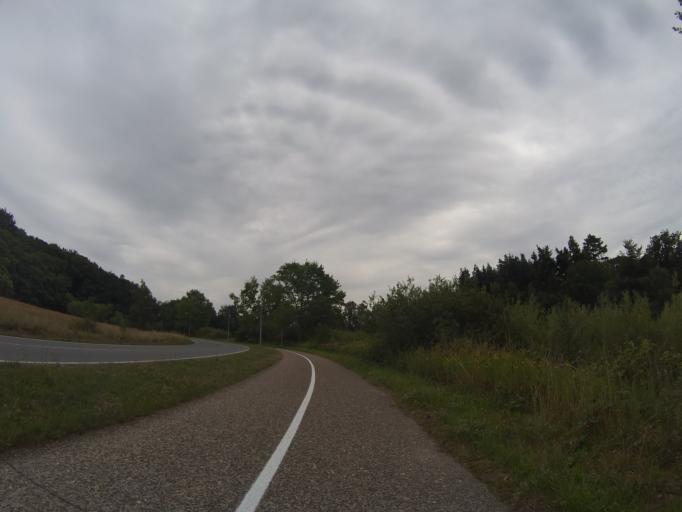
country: NL
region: North Holland
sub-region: Gemeente Hilversum
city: Hilversum
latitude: 52.2194
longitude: 5.2122
